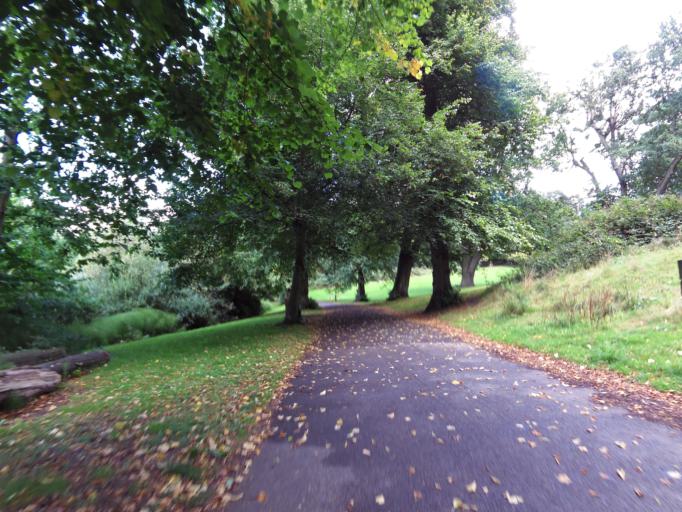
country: GB
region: England
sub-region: Suffolk
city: Ipswich
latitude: 52.0480
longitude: 1.1729
